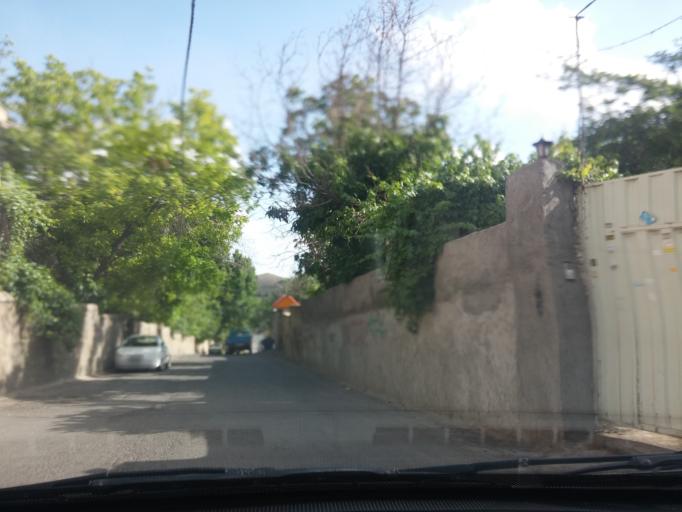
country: IR
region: Tehran
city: Damavand
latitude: 35.7313
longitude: 51.9065
